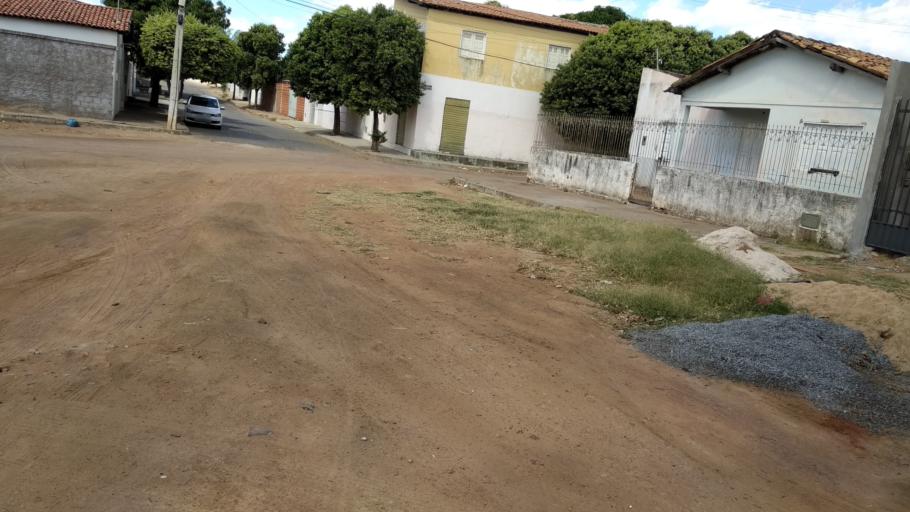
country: BR
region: Bahia
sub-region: Guanambi
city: Guanambi
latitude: -14.2341
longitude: -42.7751
